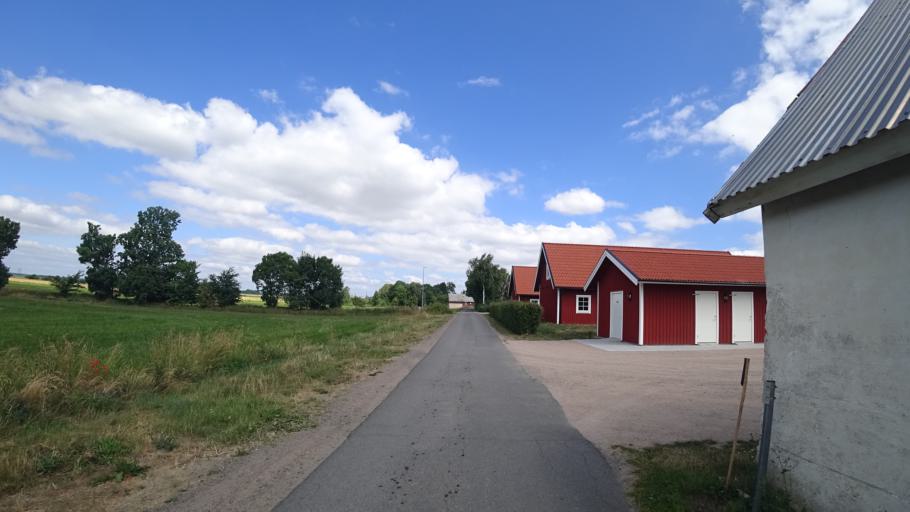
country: SE
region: Skane
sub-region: Kristianstads Kommun
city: Ahus
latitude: 55.9806
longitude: 14.2656
